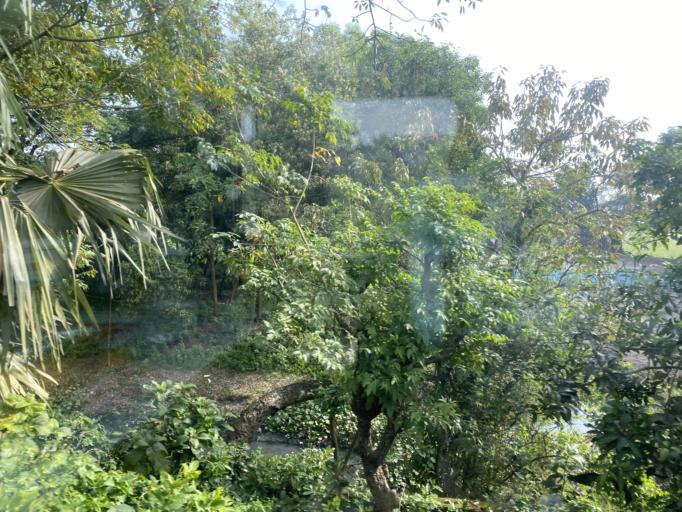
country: BD
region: Chittagong
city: Nabinagar
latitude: 23.9589
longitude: 91.1194
